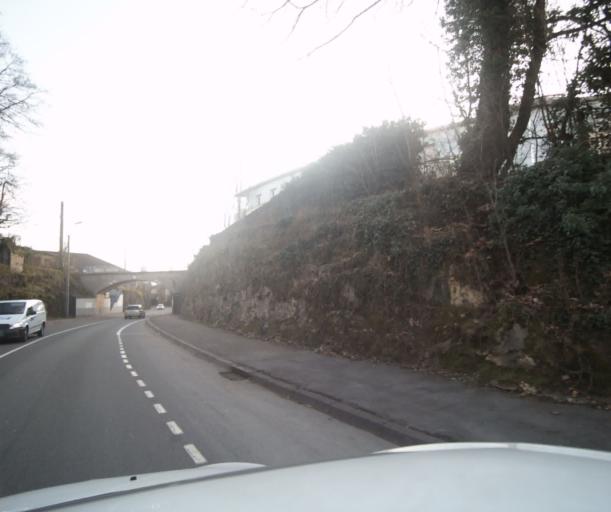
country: FR
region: Franche-Comte
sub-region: Departement du Doubs
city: Besancon
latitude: 47.2545
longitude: 6.0123
